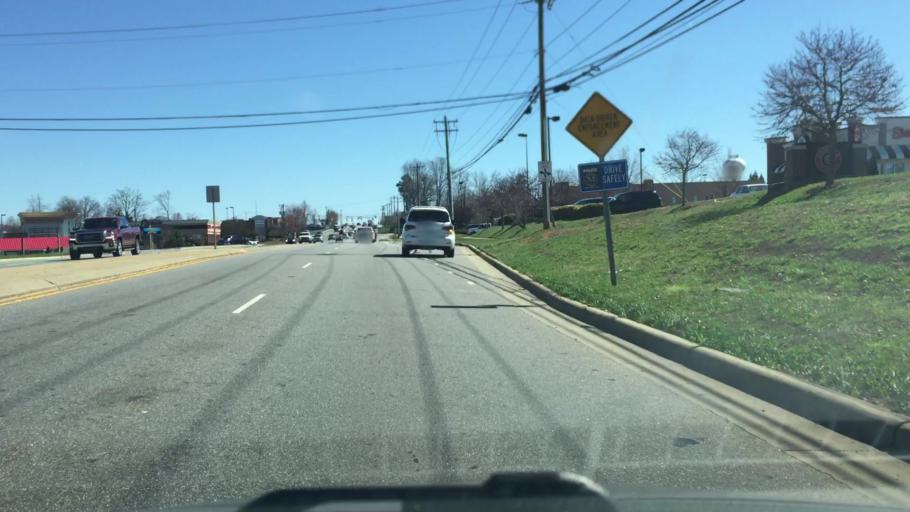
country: US
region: North Carolina
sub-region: Iredell County
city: Mooresville
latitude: 35.5959
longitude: -80.8758
